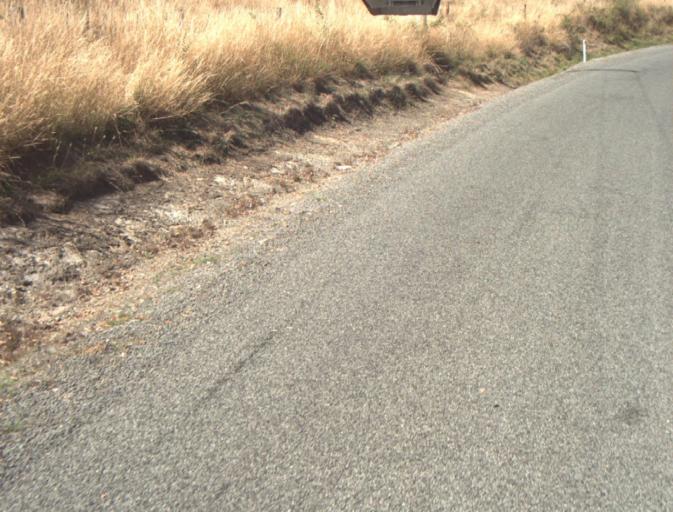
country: AU
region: Tasmania
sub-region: Launceston
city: Newstead
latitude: -41.3577
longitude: 147.3029
